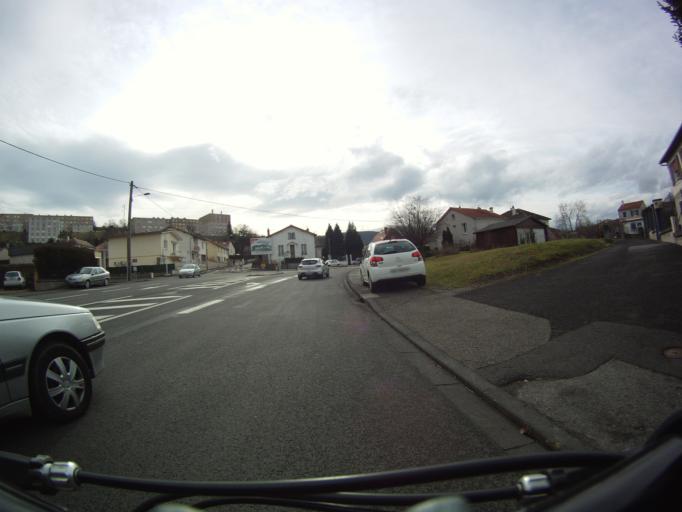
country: FR
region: Auvergne
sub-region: Departement du Puy-de-Dome
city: Aubiere
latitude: 45.7467
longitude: 3.1092
